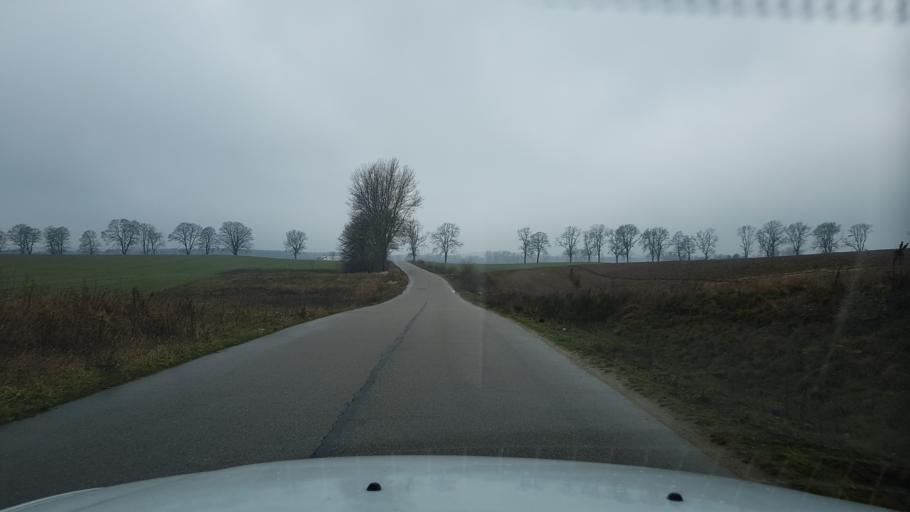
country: PL
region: West Pomeranian Voivodeship
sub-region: Powiat drawski
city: Czaplinek
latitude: 53.5785
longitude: 16.2433
